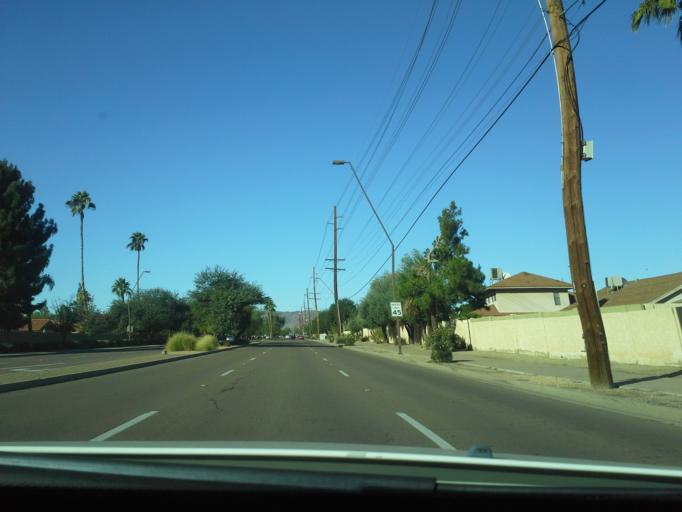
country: US
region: Arizona
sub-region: Maricopa County
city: Guadalupe
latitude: 33.3492
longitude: -111.9202
